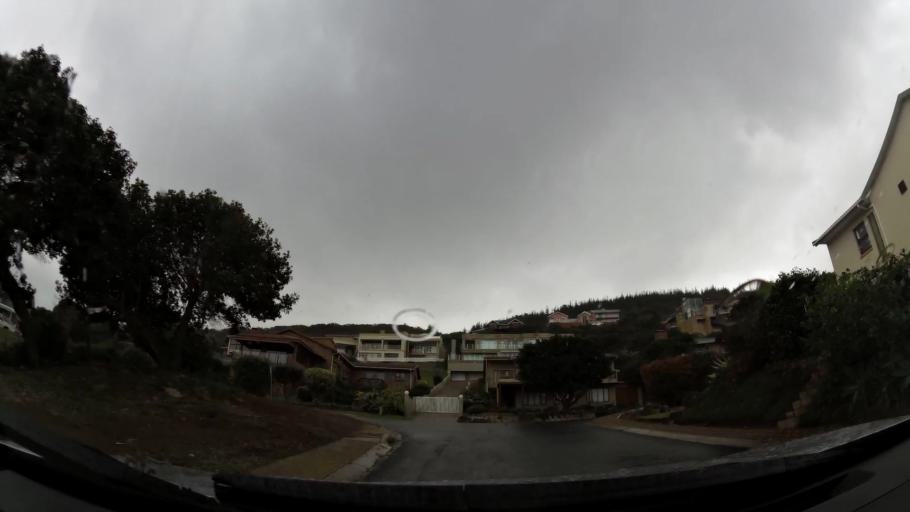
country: ZA
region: Western Cape
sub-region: Eden District Municipality
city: George
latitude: -34.0479
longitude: 22.2892
